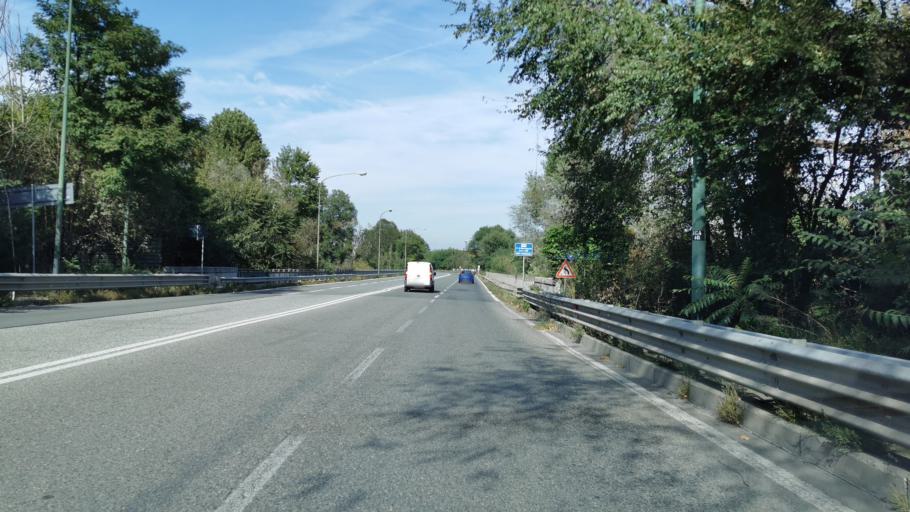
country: IT
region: Piedmont
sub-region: Provincia di Torino
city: Venaria Reale
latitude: 45.1188
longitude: 7.6608
